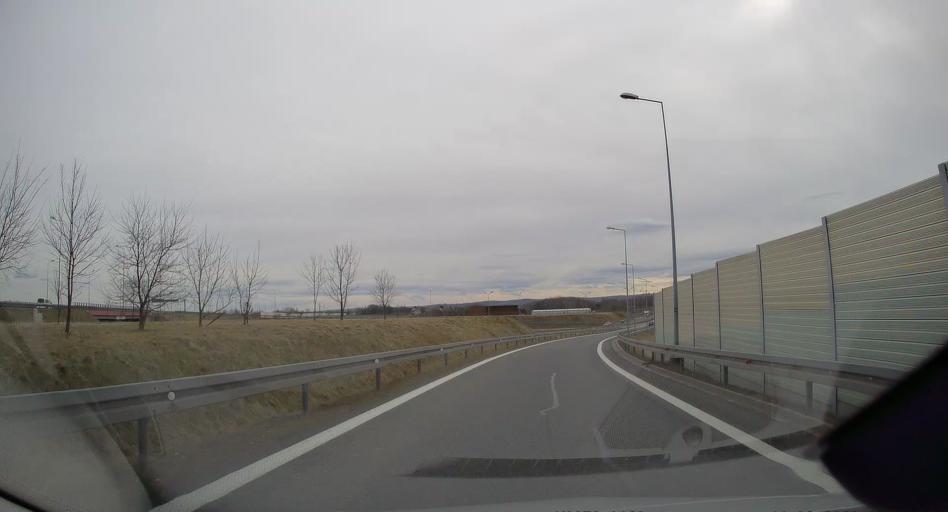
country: PL
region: Lesser Poland Voivodeship
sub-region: Powiat wielicki
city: Szarow
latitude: 49.9905
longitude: 20.2757
